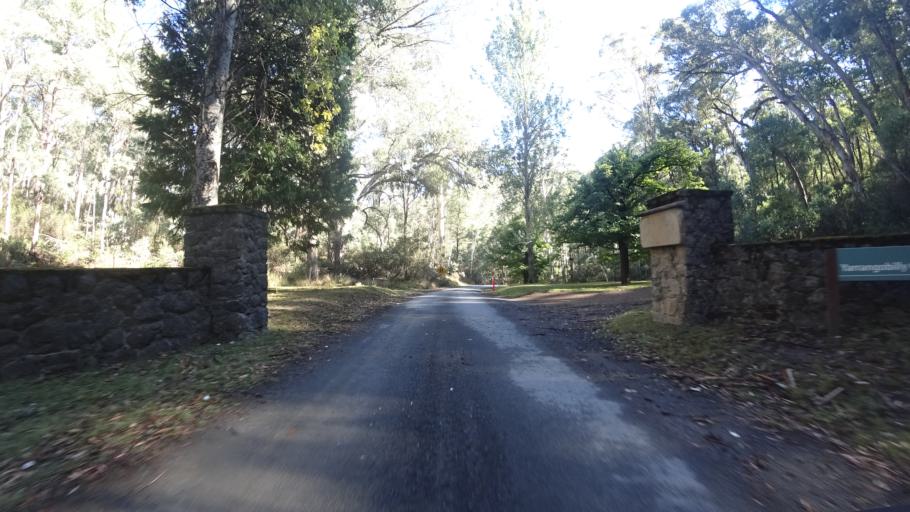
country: AU
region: New South Wales
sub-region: Tumut Shire
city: Tumut
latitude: -35.7259
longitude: 148.4963
